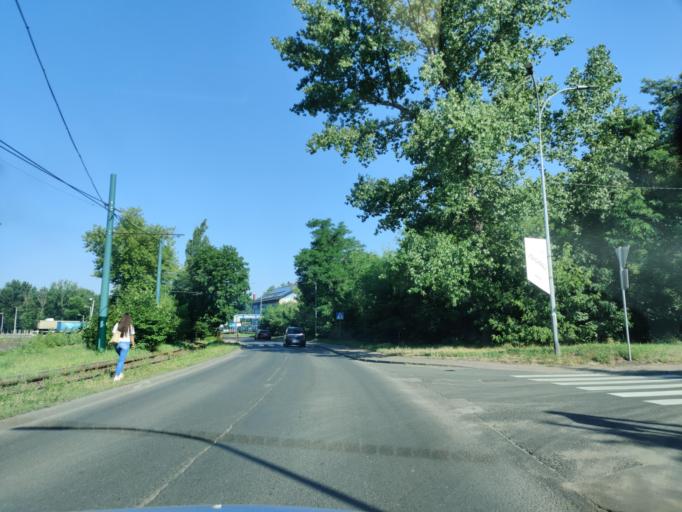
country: PL
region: Silesian Voivodeship
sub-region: Sosnowiec
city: Sosnowiec
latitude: 50.2518
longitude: 19.1286
